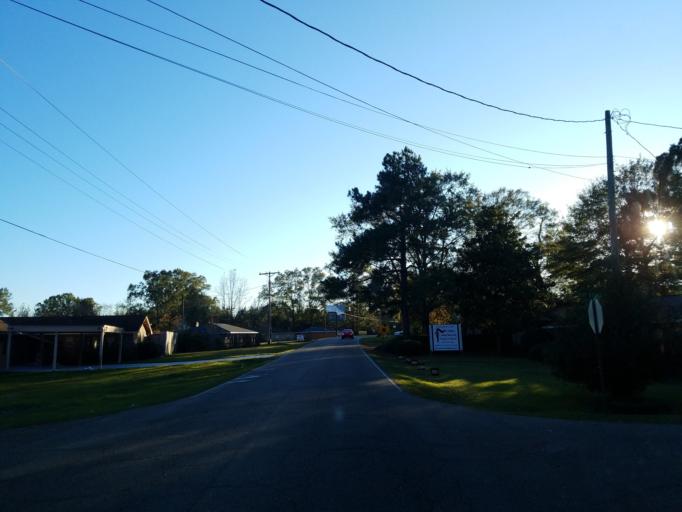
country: US
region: Mississippi
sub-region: Lamar County
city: Arnold Line
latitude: 31.3335
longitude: -89.3675
